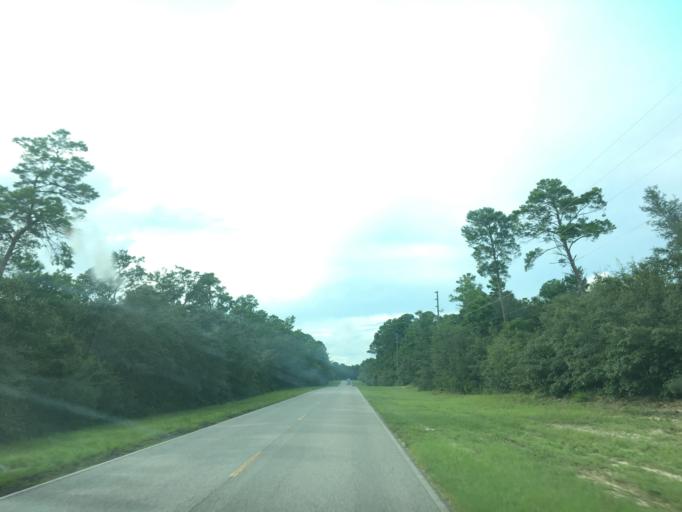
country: US
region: Florida
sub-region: Wakulla County
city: Crawfordville
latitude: 29.9228
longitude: -84.3738
